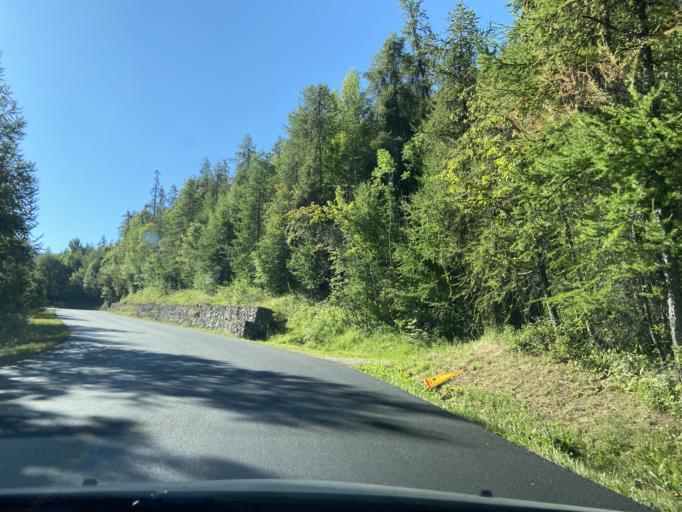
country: FR
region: Provence-Alpes-Cote d'Azur
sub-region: Departement des Hautes-Alpes
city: Guillestre
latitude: 44.6353
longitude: 6.6298
